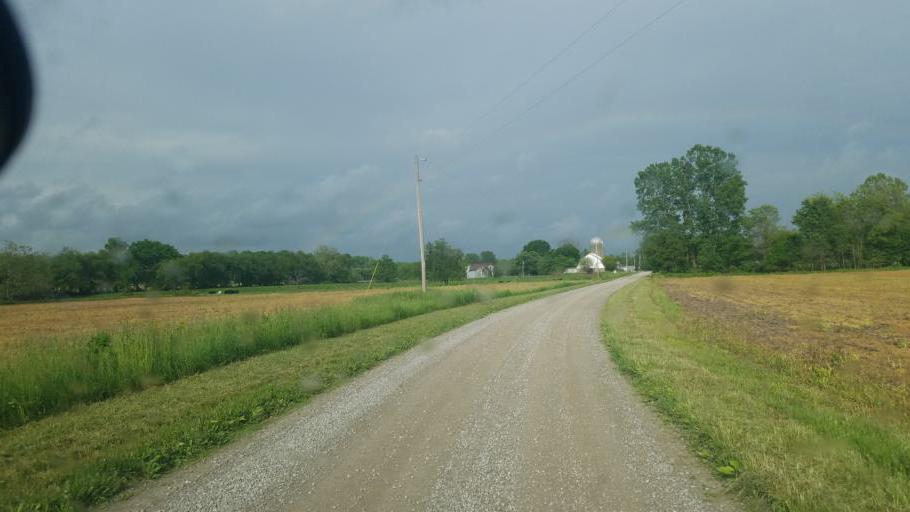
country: US
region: Ohio
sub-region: Knox County
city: Fredericktown
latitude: 40.5115
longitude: -82.6488
